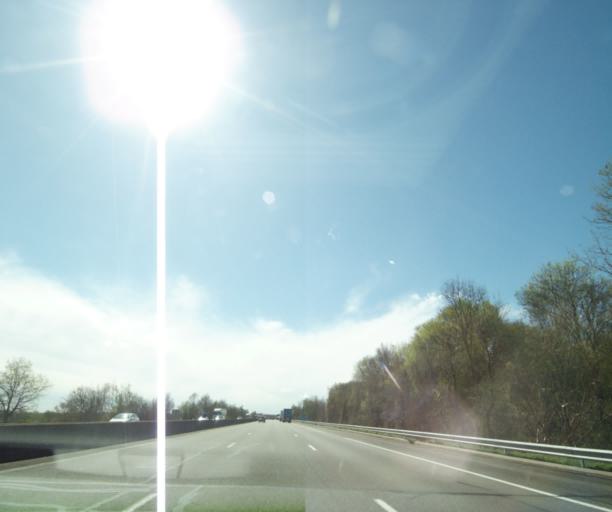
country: FR
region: Bourgogne
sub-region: Departement de Saone-et-Loire
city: Romaneche-Thorins
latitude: 46.1673
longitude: 4.7704
